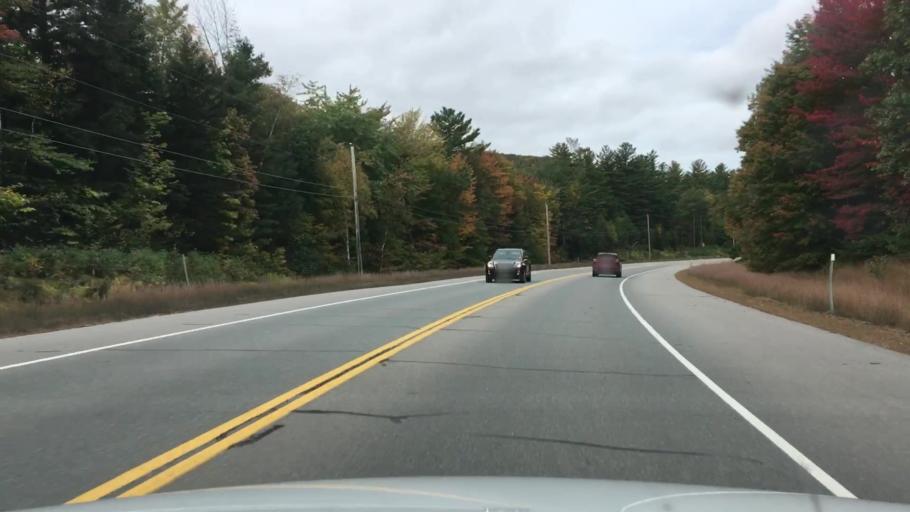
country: US
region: New Hampshire
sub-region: Coos County
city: Gorham
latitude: 44.3924
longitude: -71.0459
